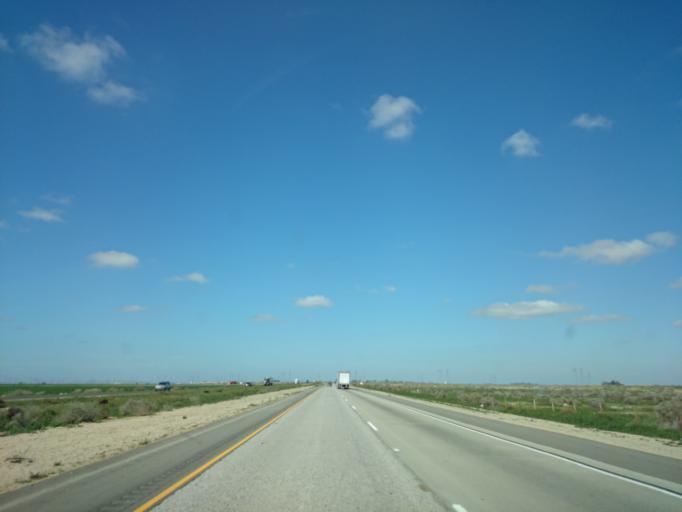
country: US
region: California
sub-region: Kern County
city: Buttonwillow
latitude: 35.3738
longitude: -119.3624
